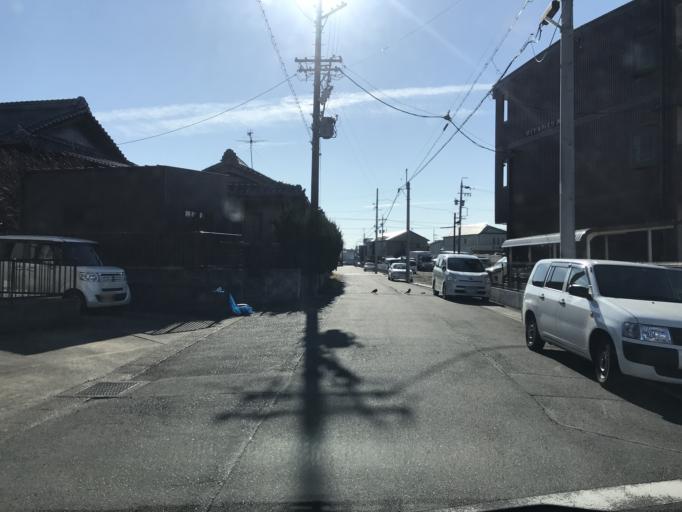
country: JP
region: Aichi
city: Nagoya-shi
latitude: 35.2166
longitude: 136.8525
